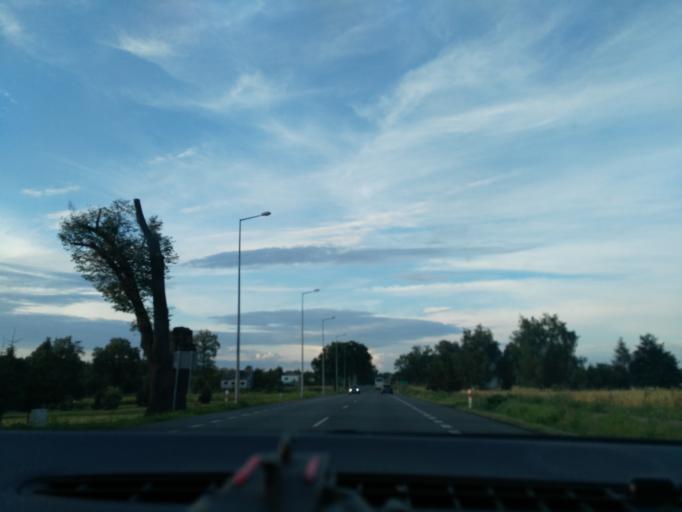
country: PL
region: Lublin Voivodeship
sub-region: Powiat lubelski
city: Niedrzwica Duza
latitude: 51.0989
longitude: 22.3704
